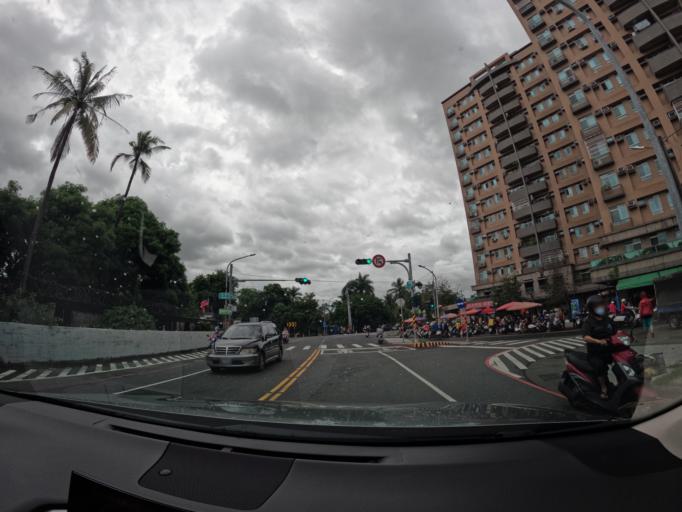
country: TW
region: Taiwan
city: Fengshan
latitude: 22.6300
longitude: 120.3735
